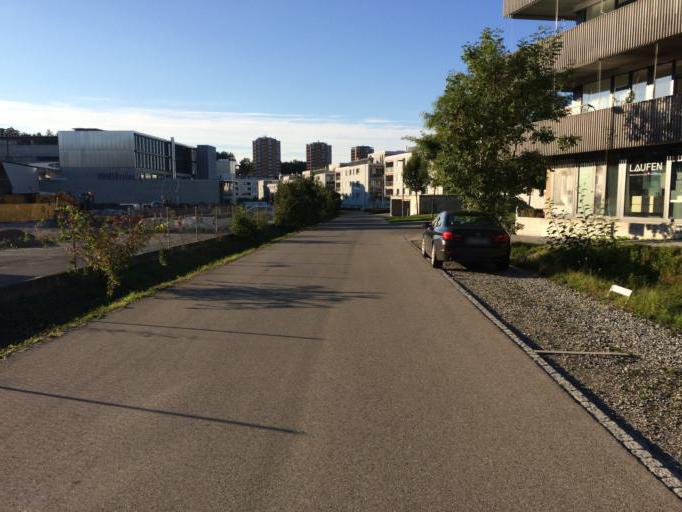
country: CH
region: Bern
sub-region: Bern-Mittelland District
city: Koniz
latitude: 46.9342
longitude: 7.4199
